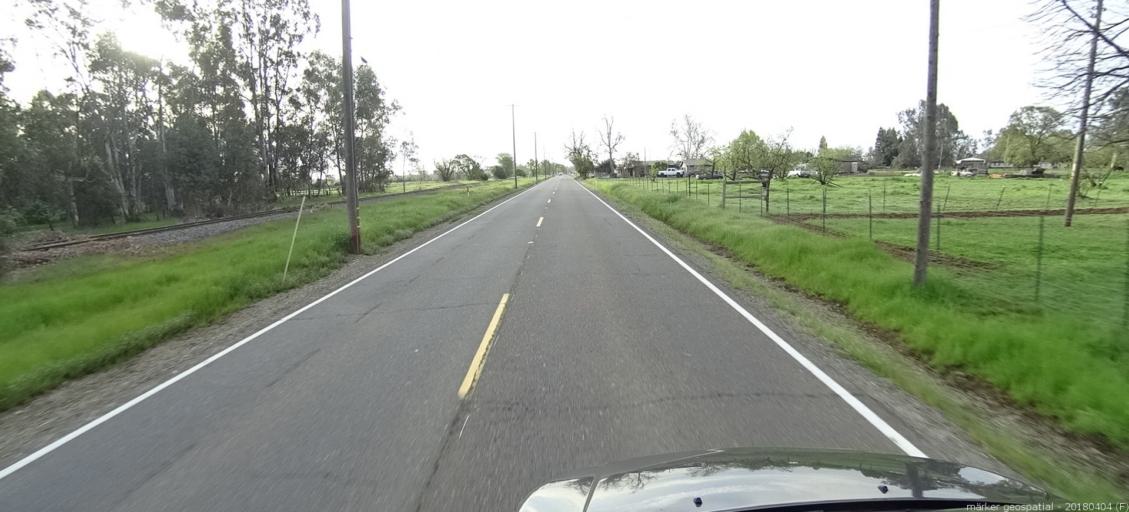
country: US
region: California
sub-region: Sacramento County
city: Wilton
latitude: 38.4037
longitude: -121.2606
